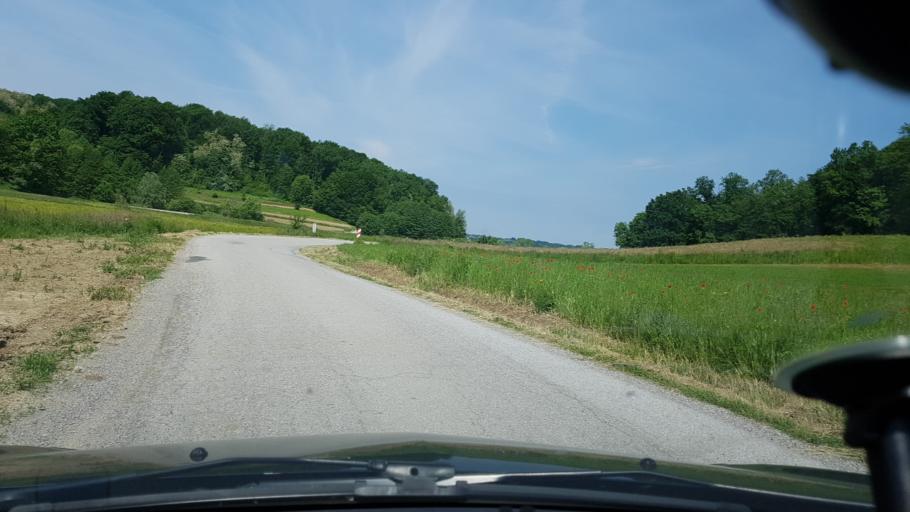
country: HR
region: Krapinsko-Zagorska
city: Selnica
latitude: 46.0318
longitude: 16.0310
